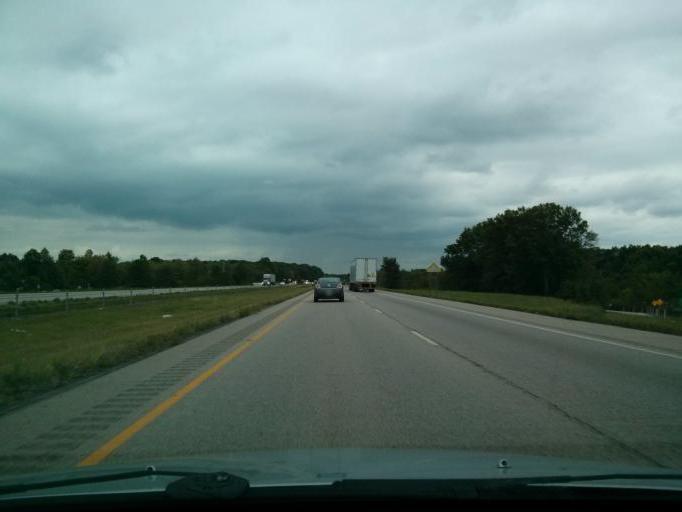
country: US
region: Ohio
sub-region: Mahoning County
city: Craig Beach
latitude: 41.1059
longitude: -81.0540
